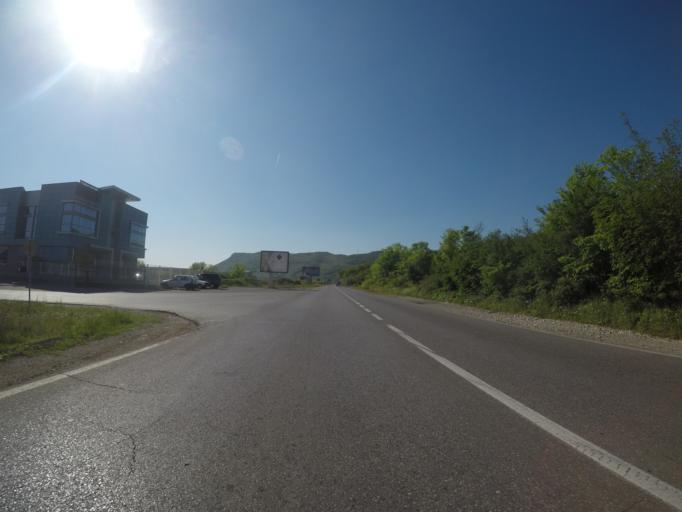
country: ME
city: Spuz
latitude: 42.4716
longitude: 19.1732
